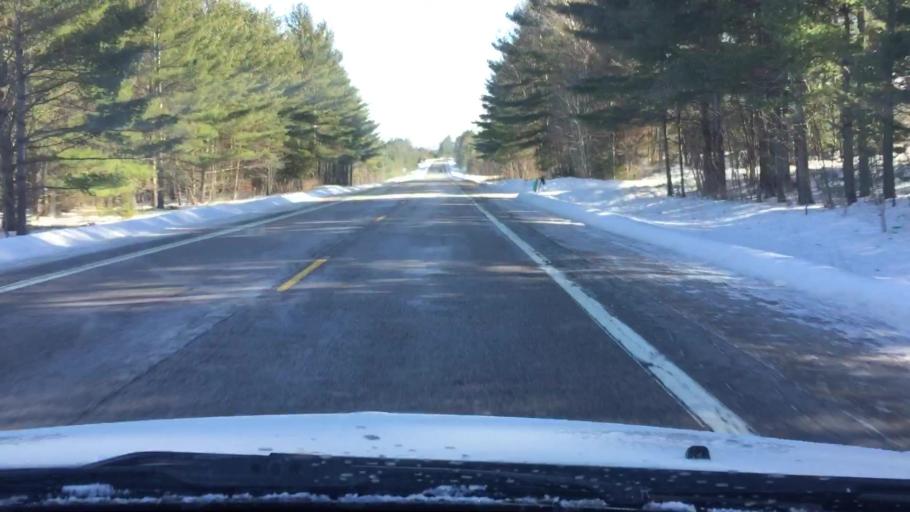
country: US
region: Michigan
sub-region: Charlevoix County
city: East Jordan
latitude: 45.0975
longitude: -85.1072
